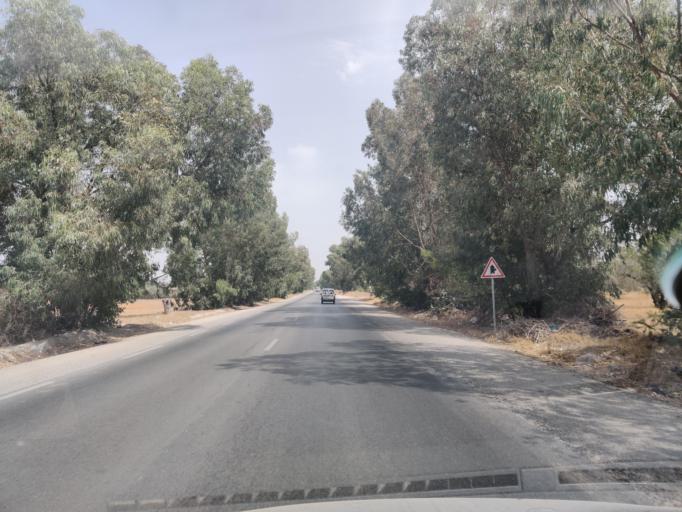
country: TN
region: Nabul
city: Al Hammamat
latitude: 36.4451
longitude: 10.5727
